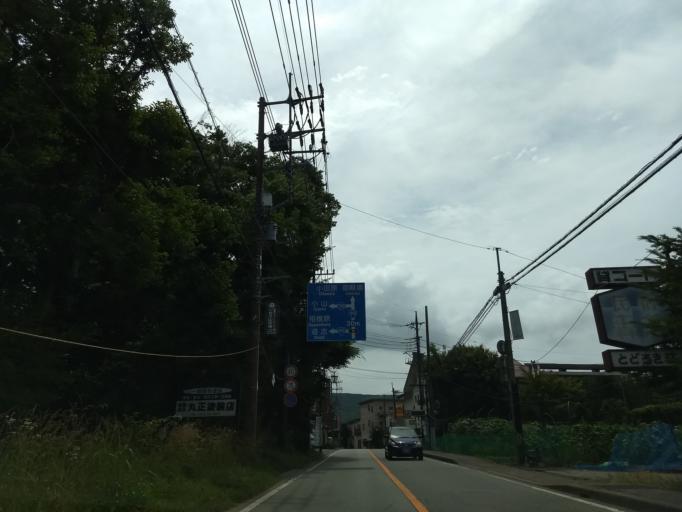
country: JP
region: Shizuoka
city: Gotemba
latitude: 35.4272
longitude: 138.9019
